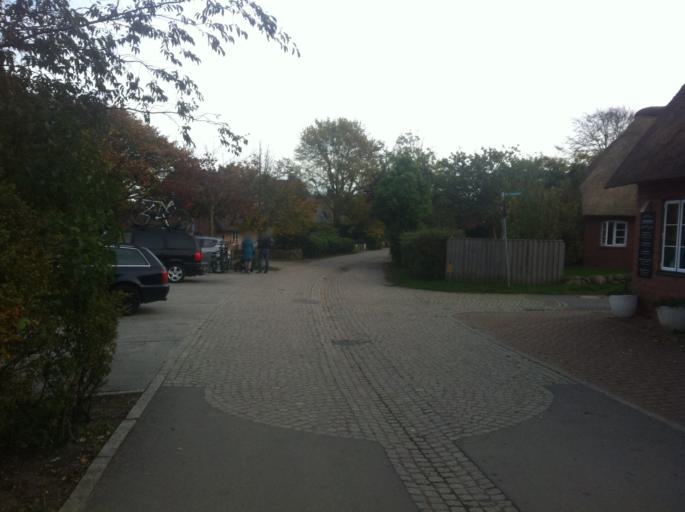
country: DE
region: Schleswig-Holstein
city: Nebel
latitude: 54.6529
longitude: 8.3549
